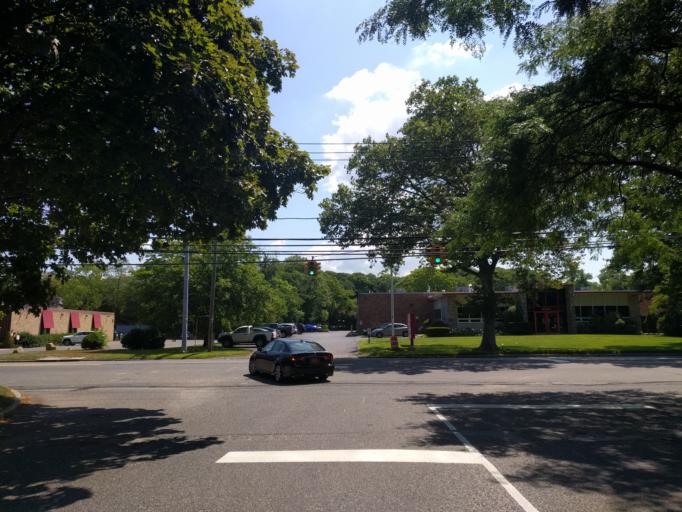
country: US
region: New York
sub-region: Suffolk County
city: Hauppauge
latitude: 40.8128
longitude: -73.2334
